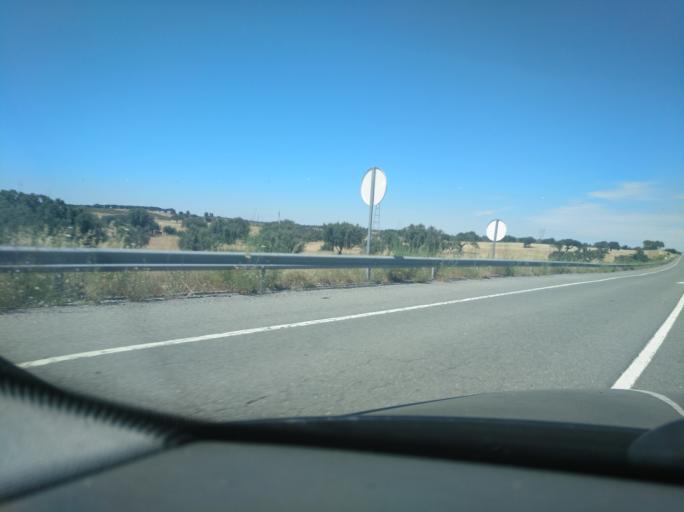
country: PT
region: Beja
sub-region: Ourique
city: Ourique
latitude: 37.6631
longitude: -8.1723
